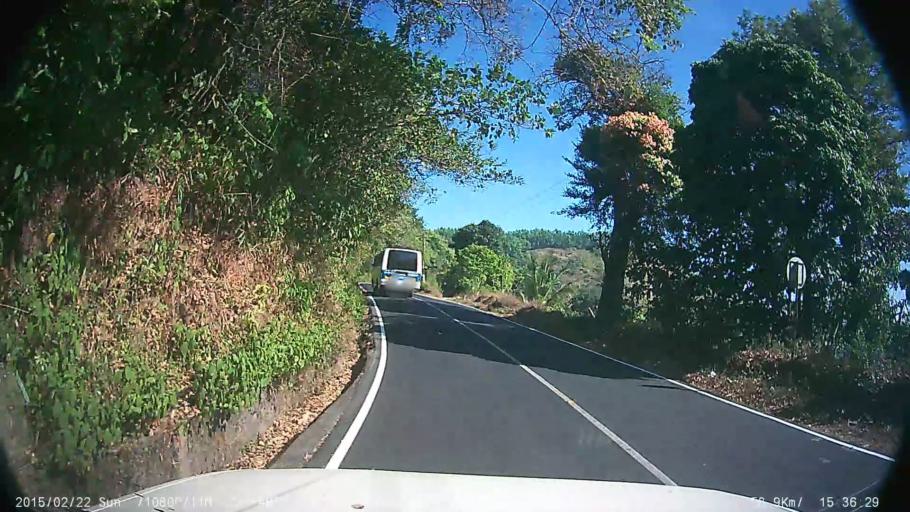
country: IN
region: Kerala
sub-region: Kottayam
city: Erattupetta
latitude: 9.5624
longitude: 76.9784
